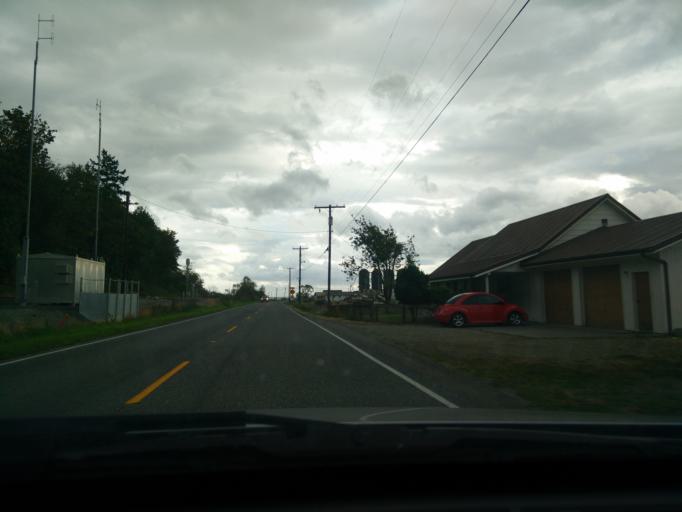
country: US
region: Washington
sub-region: Snohomish County
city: Stanwood
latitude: 48.2718
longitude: -122.3653
